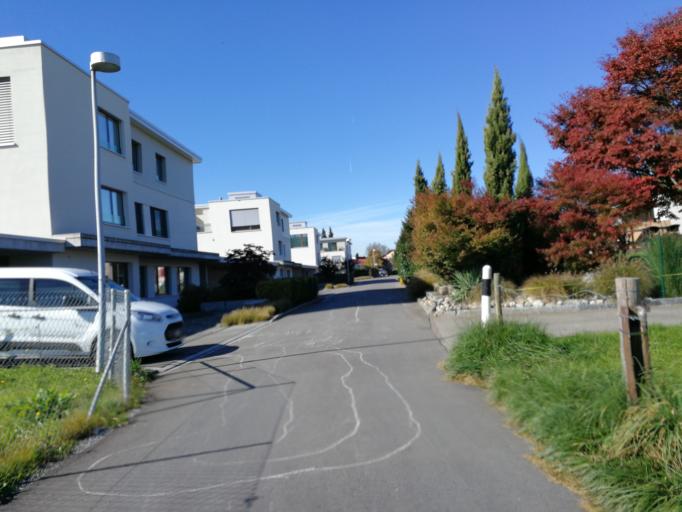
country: CH
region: Saint Gallen
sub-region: Wahlkreis See-Gaster
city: Jona
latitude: 47.2193
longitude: 8.8362
